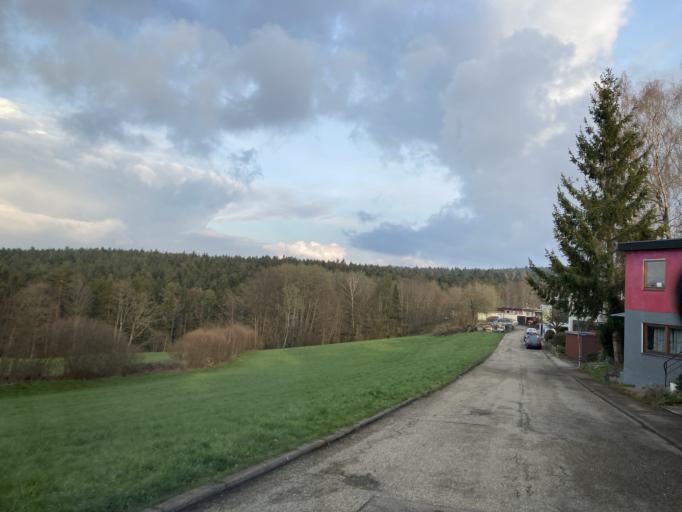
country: DE
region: Baden-Wuerttemberg
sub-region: Karlsruhe Region
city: Schomberg
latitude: 48.7941
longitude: 8.6522
